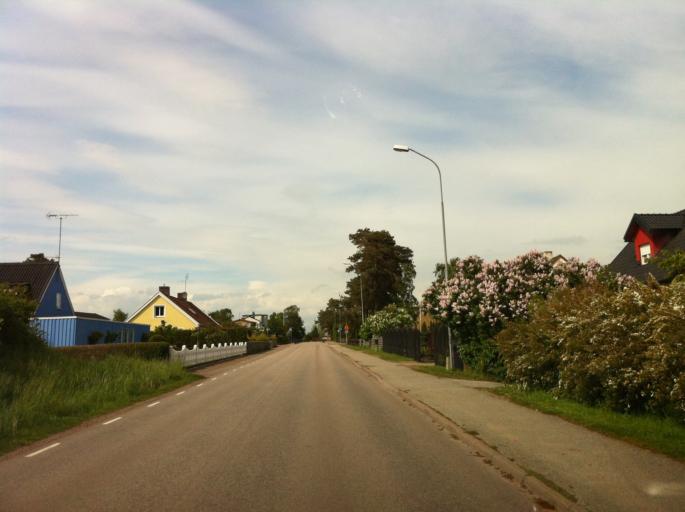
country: SE
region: Skane
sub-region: Landskrona
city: Asmundtorp
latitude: 55.8538
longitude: 12.9109
